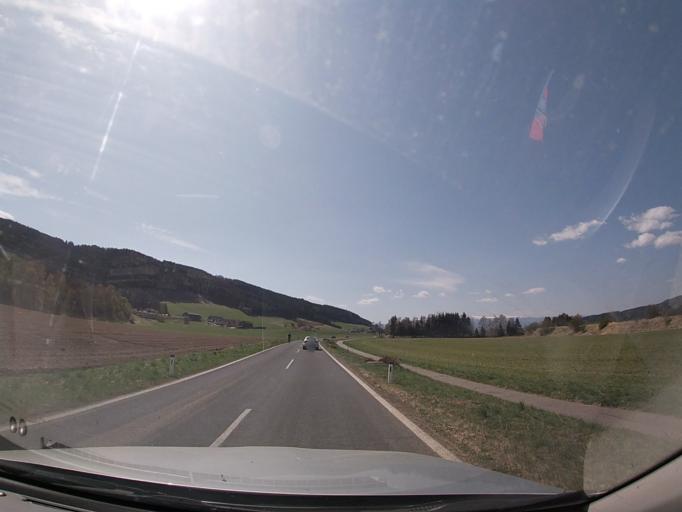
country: AT
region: Styria
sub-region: Politischer Bezirk Murtal
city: Sankt Lorenzen bei Knittelfeld
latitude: 47.2397
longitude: 14.8756
